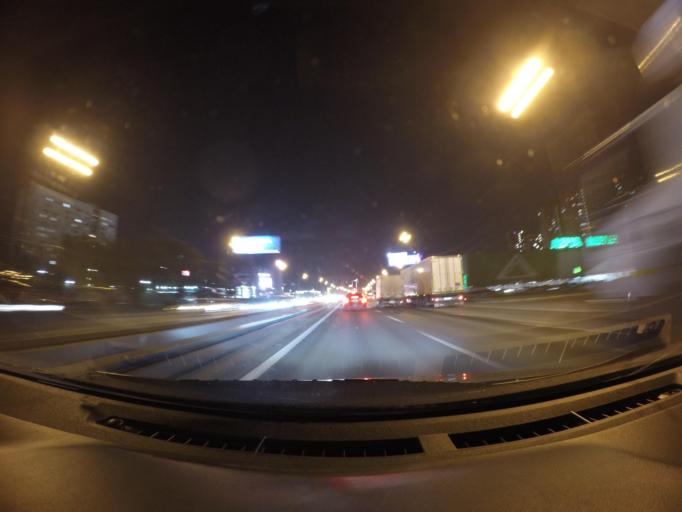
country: RU
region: Moscow
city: Khimki
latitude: 55.9054
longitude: 37.4147
